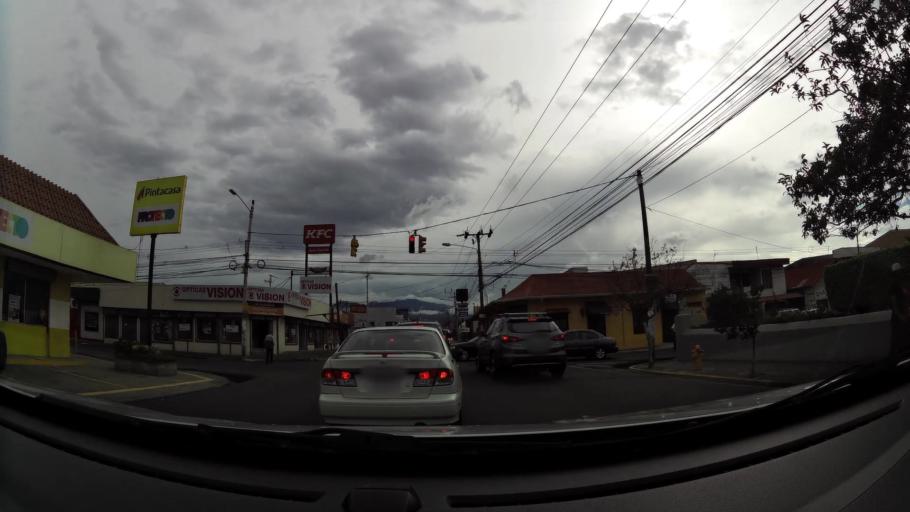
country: CR
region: San Jose
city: San Juan
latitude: 9.9623
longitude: -84.0776
